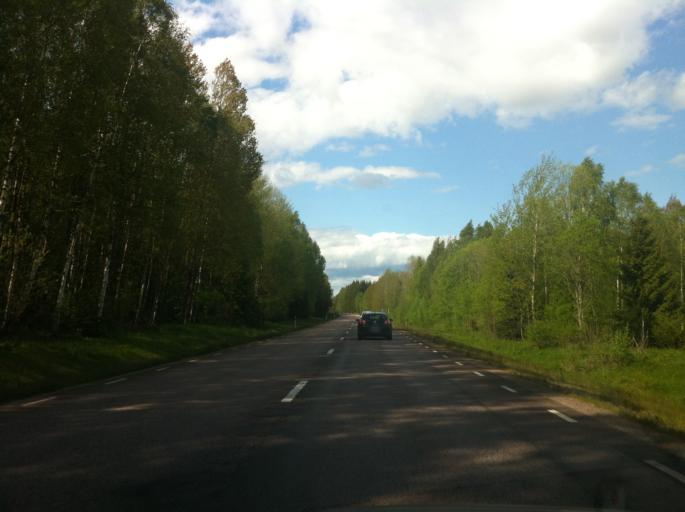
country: SE
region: Vaermland
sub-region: Kristinehamns Kommun
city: Bjorneborg
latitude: 59.2184
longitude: 14.1839
